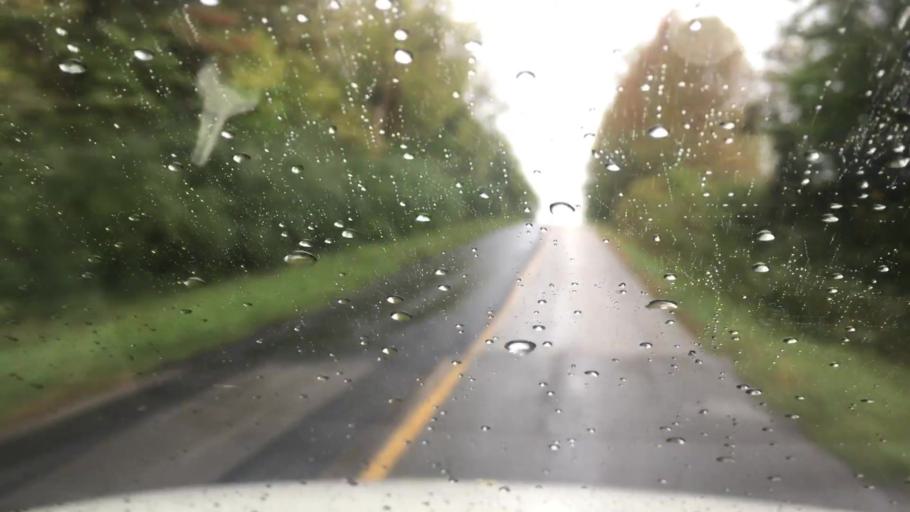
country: US
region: Missouri
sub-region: Boone County
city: Columbia
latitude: 38.9384
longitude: -92.4966
